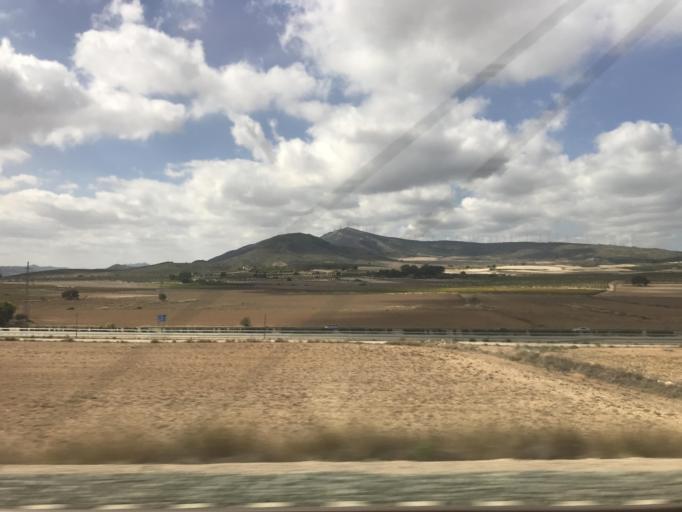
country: ES
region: Castille-La Mancha
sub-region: Provincia de Albacete
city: Caudete
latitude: 38.7629
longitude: -0.9555
